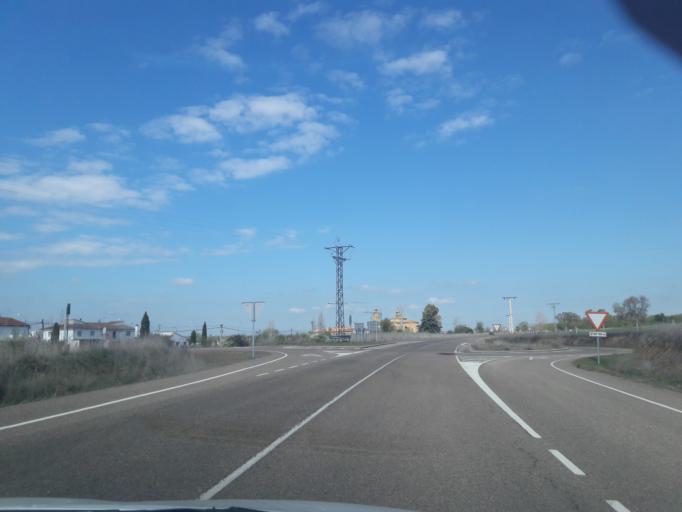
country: ES
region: Castille and Leon
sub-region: Provincia de Salamanca
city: Ciudad Rodrigo
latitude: 40.5711
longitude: -6.4893
